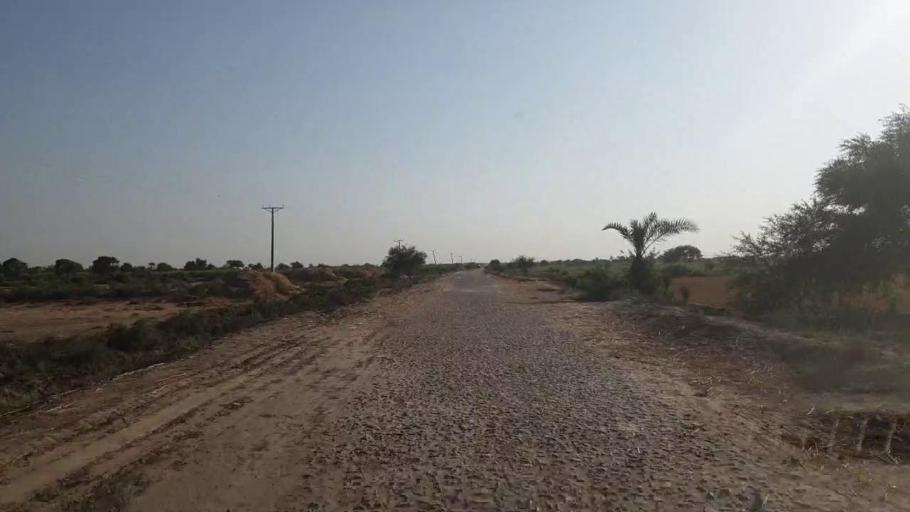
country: PK
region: Sindh
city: Talhar
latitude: 24.9405
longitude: 68.7518
